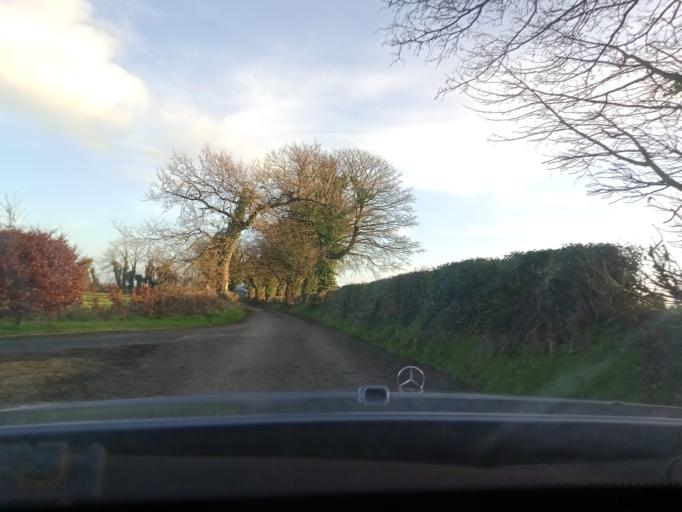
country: IE
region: Leinster
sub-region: Kilkenny
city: Callan
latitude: 52.4742
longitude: -7.4351
